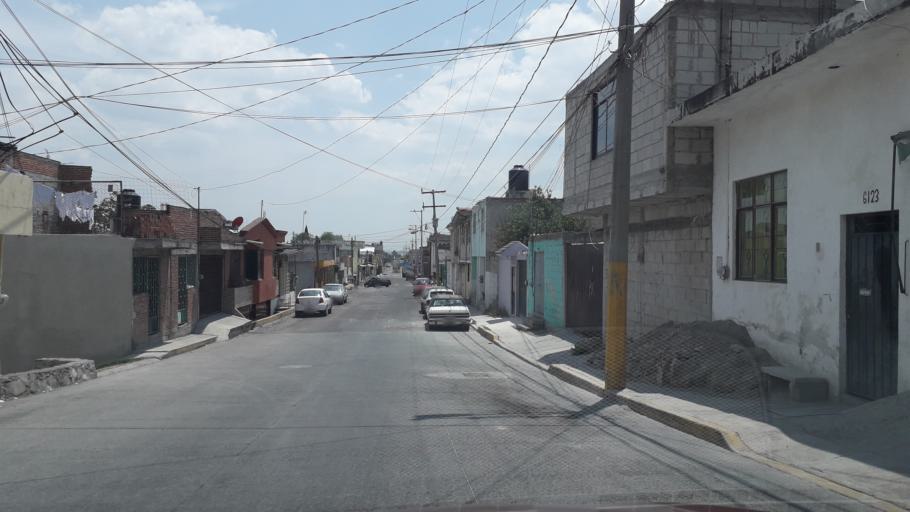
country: MX
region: Puebla
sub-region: Puebla
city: Galaxia la Calera
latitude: 18.9960
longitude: -98.1824
